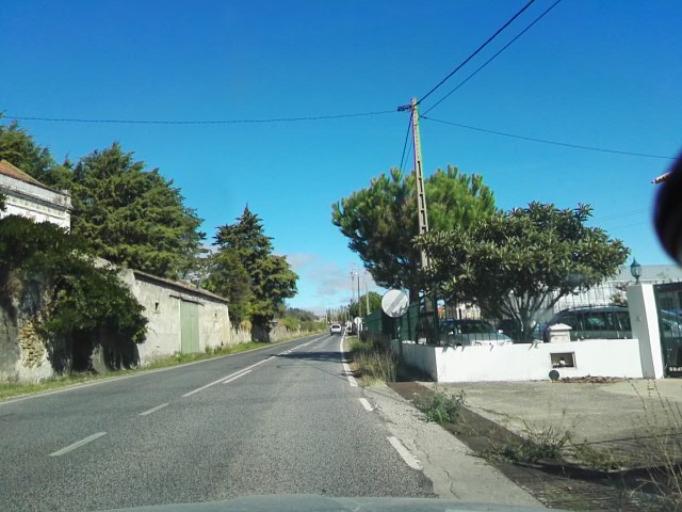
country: PT
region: Lisbon
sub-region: Arruda Dos Vinhos
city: Arruda dos Vinhos
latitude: 38.9742
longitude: -9.0669
